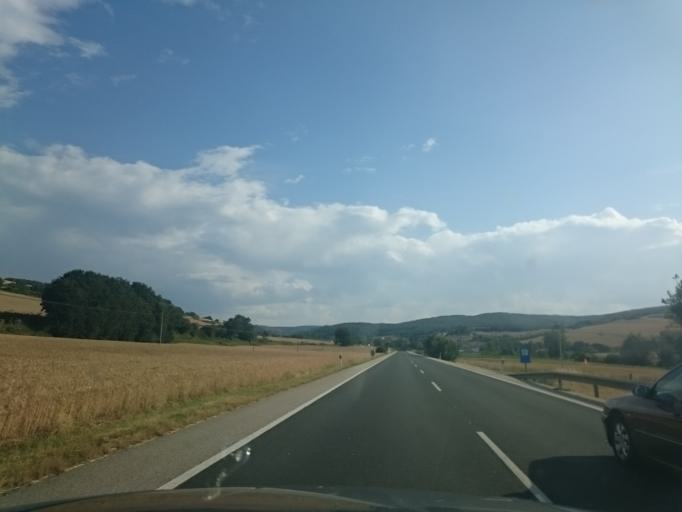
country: ES
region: Castille and Leon
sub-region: Provincia de Burgos
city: Espinosa del Camino
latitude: 42.3961
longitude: -3.3019
